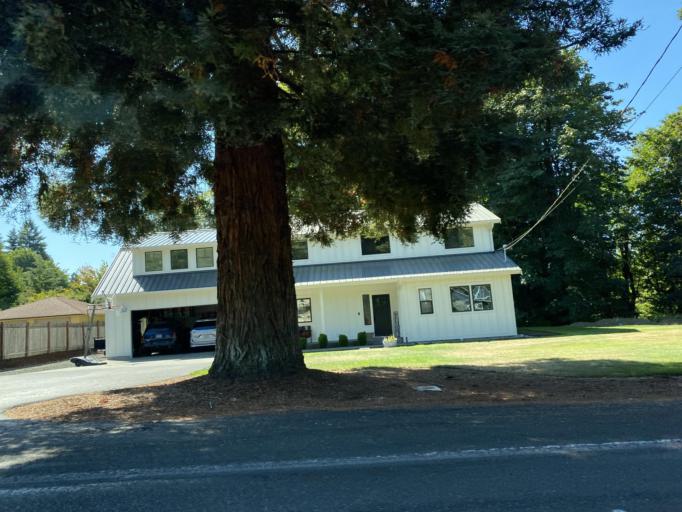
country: US
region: Washington
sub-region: Thurston County
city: Olympia
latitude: 47.0296
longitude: -122.8831
